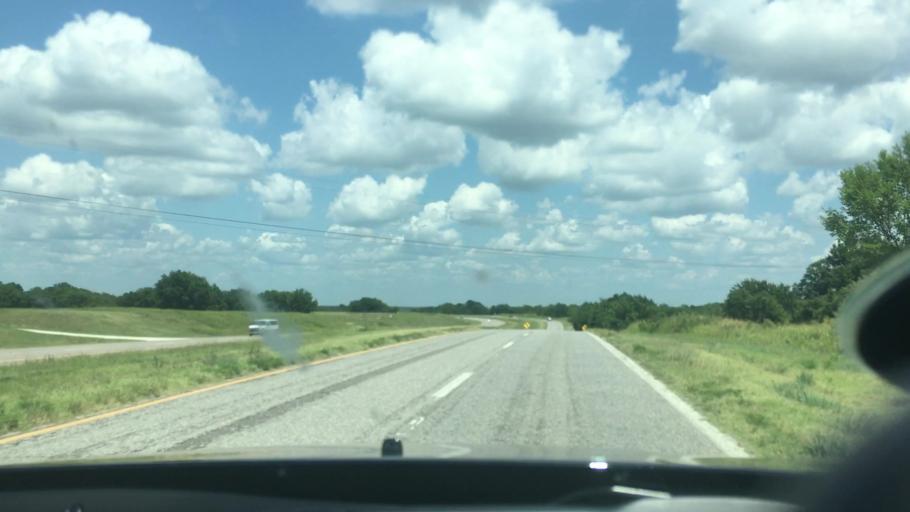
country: US
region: Oklahoma
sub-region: Pontotoc County
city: Ada
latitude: 34.6884
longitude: -96.7506
